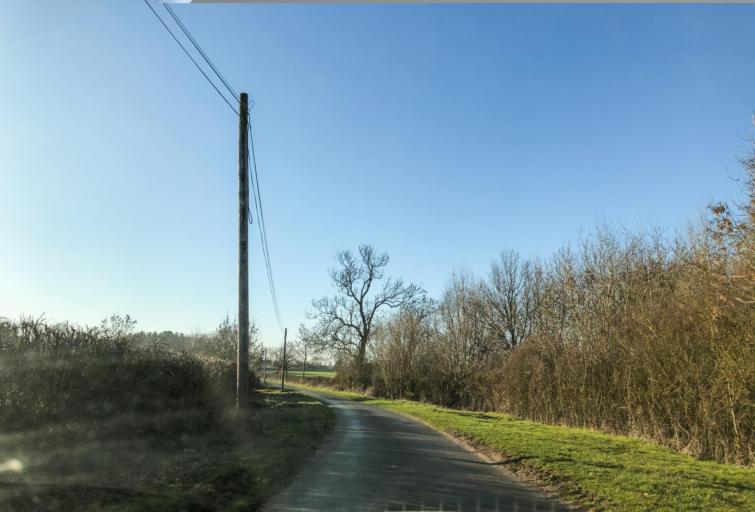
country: GB
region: England
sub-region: Warwickshire
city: Warwick
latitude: 52.2406
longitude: -1.5759
